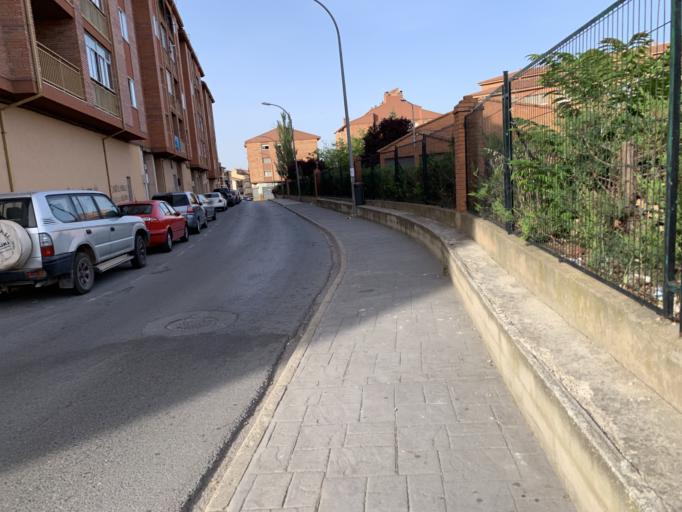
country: ES
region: Aragon
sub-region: Provincia de Teruel
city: Teruel
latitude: 40.3503
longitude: -1.1109
